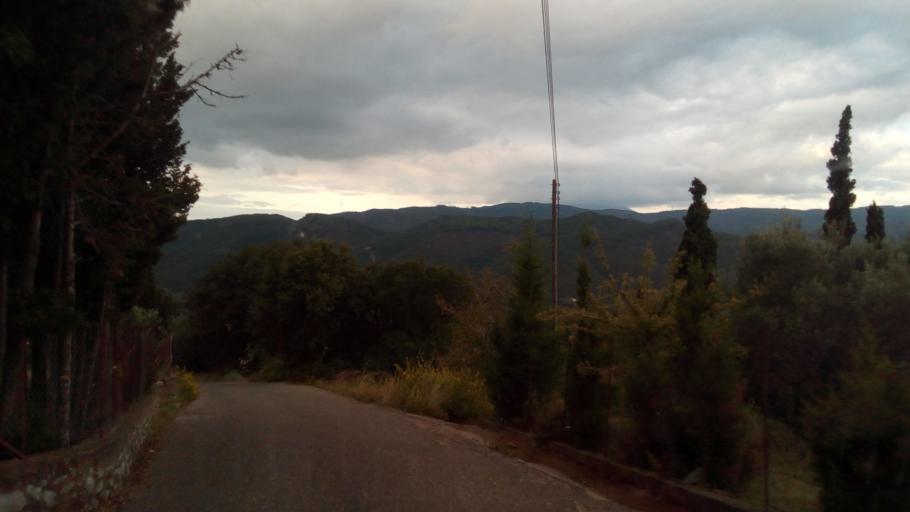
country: GR
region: West Greece
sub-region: Nomos Aitolias kai Akarnanias
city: Nafpaktos
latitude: 38.4056
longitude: 21.8011
